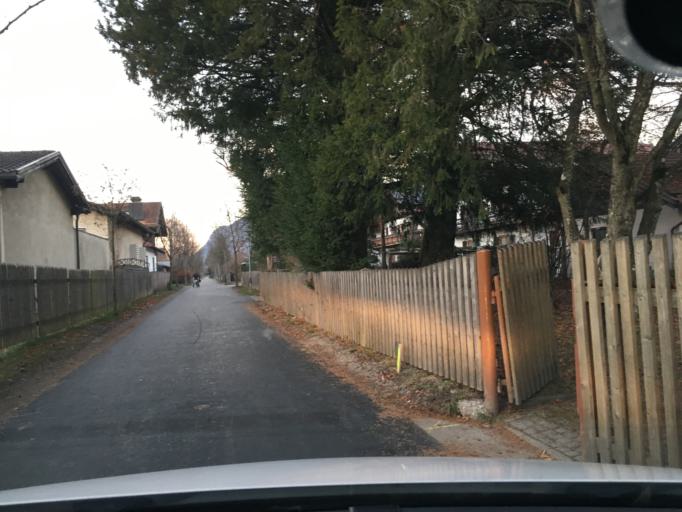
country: DE
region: Bavaria
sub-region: Upper Bavaria
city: Oberaudorf
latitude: 47.6496
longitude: 12.1737
